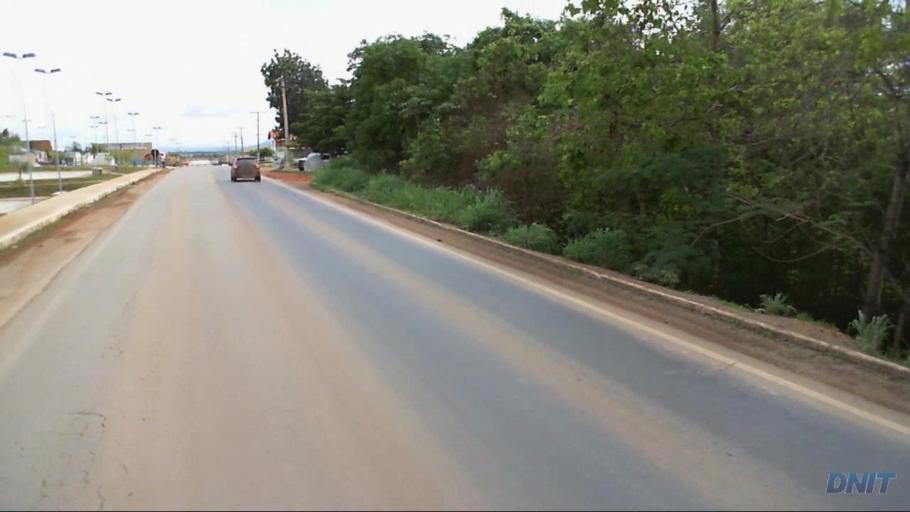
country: BR
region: Goias
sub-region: Padre Bernardo
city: Padre Bernardo
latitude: -15.1743
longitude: -48.2859
